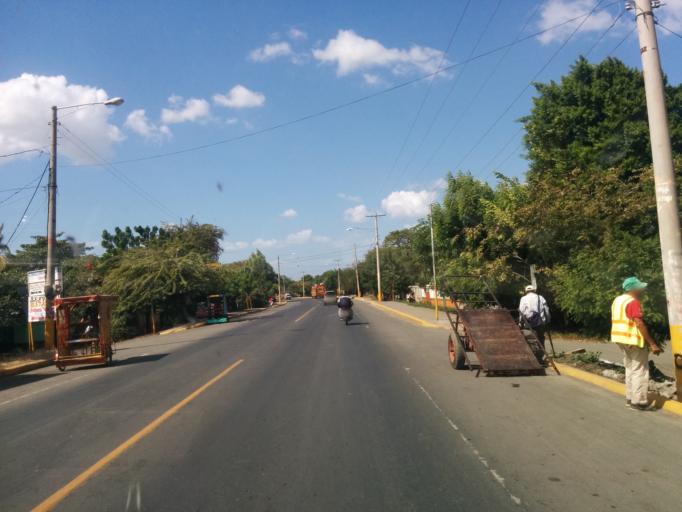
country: NI
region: Managua
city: Tipitapa
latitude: 12.1916
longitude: -86.0974
